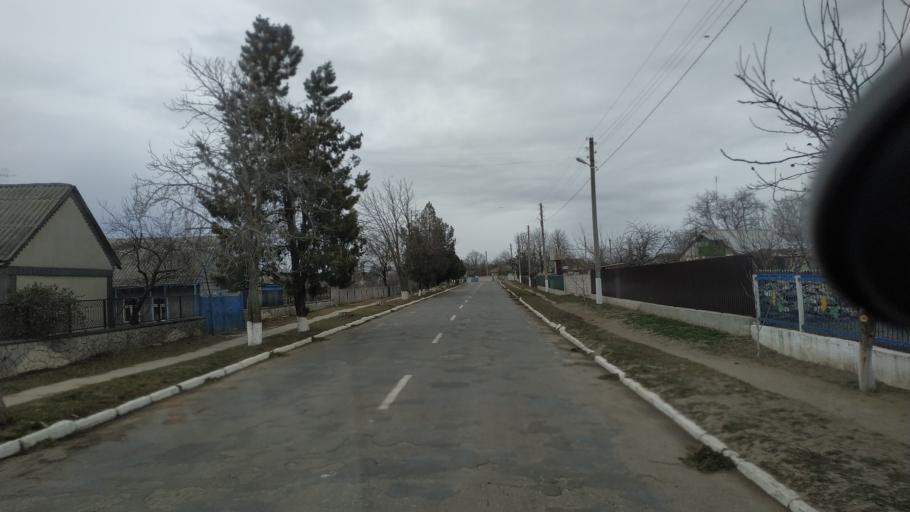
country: MD
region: Telenesti
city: Cocieri
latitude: 47.3027
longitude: 29.1134
